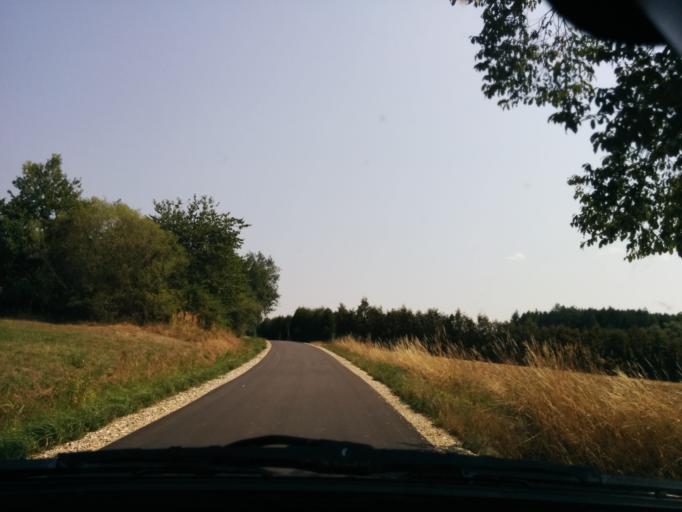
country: AT
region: Lower Austria
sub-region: Politischer Bezirk Krems
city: Krumau am Kamp
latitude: 48.6160
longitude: 15.3872
